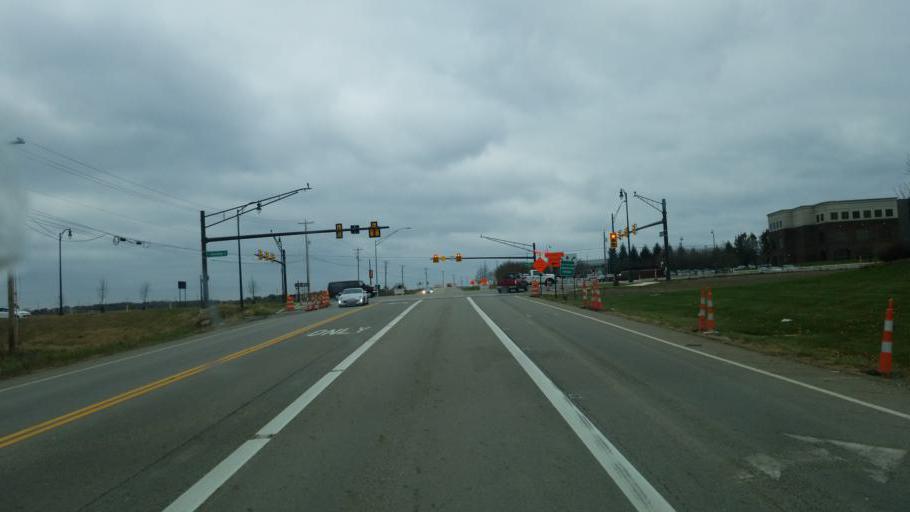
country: US
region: Ohio
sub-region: Franklin County
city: New Albany
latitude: 40.0787
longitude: -82.8509
